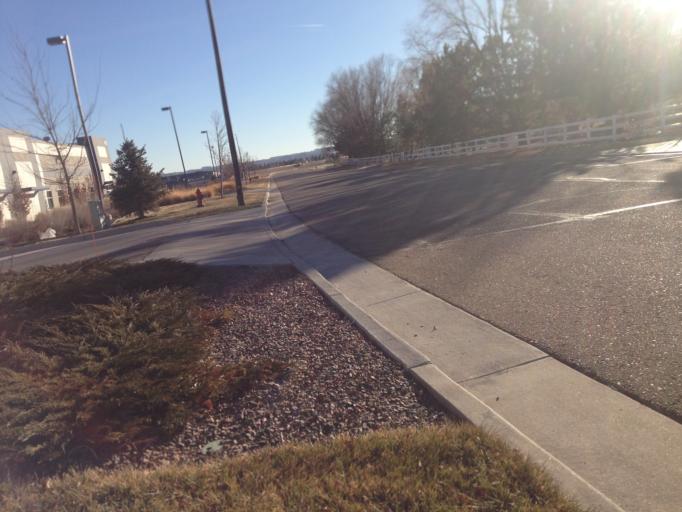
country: US
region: Colorado
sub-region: Boulder County
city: Louisville
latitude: 39.9642
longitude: -105.1121
